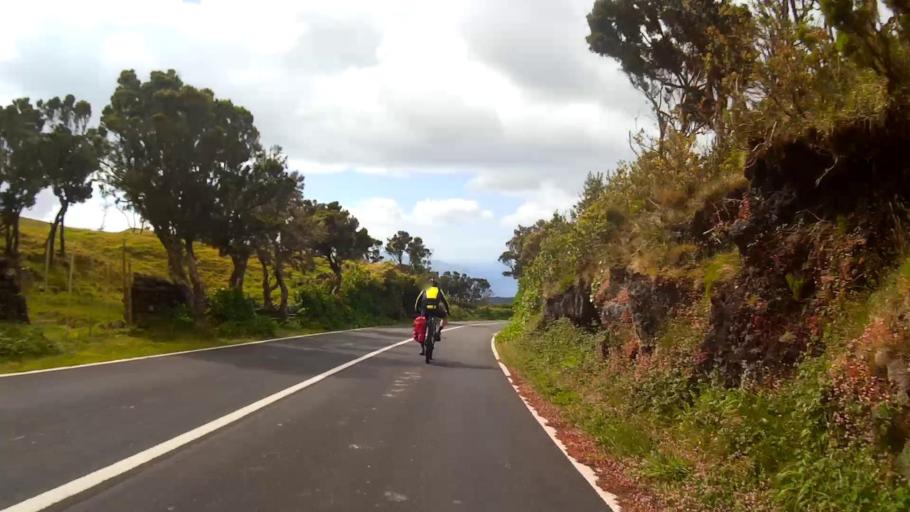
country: PT
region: Azores
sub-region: Madalena
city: Madalena
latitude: 38.4970
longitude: -28.4607
